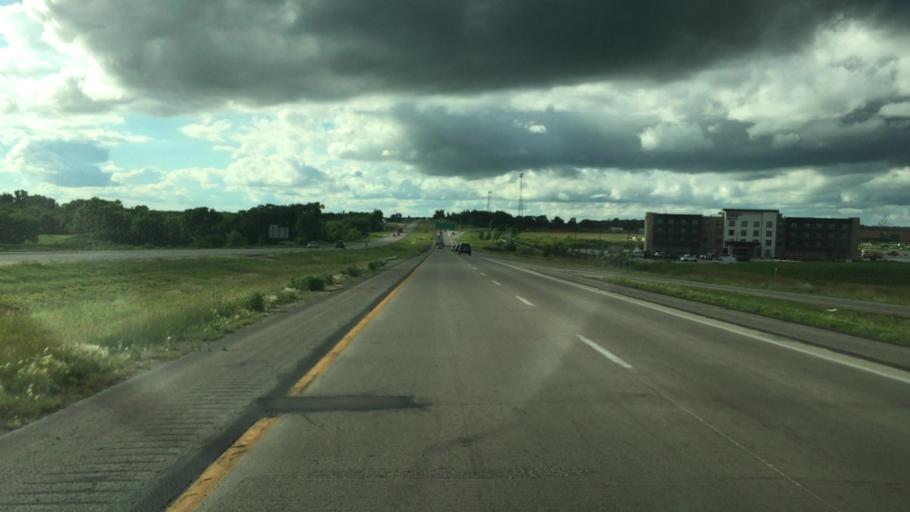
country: US
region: Iowa
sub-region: Polk County
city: Altoona
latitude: 41.6504
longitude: -93.5147
